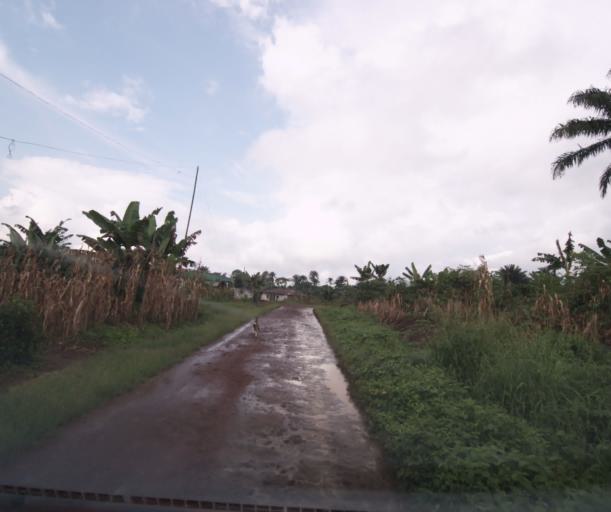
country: CM
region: Littoral
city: Melong
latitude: 5.0576
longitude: 9.9682
